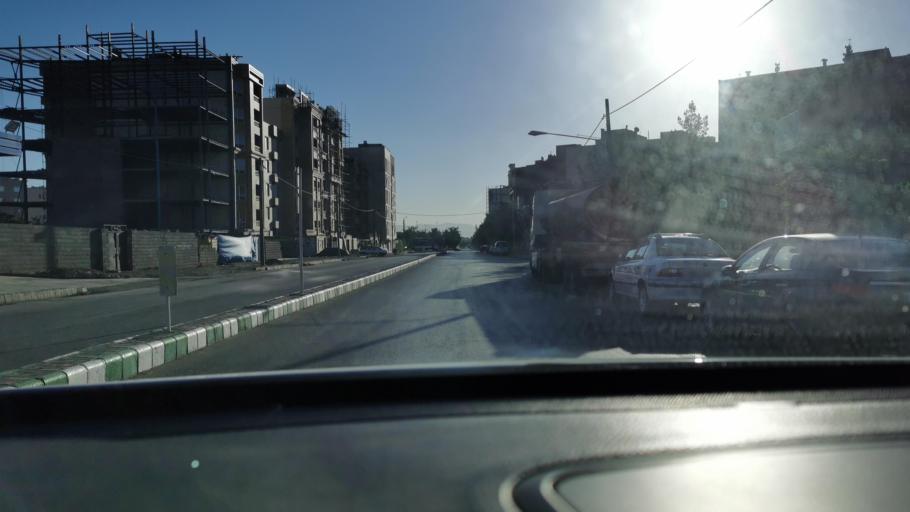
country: IR
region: Razavi Khorasan
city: Mashhad
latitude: 36.3605
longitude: 59.4840
